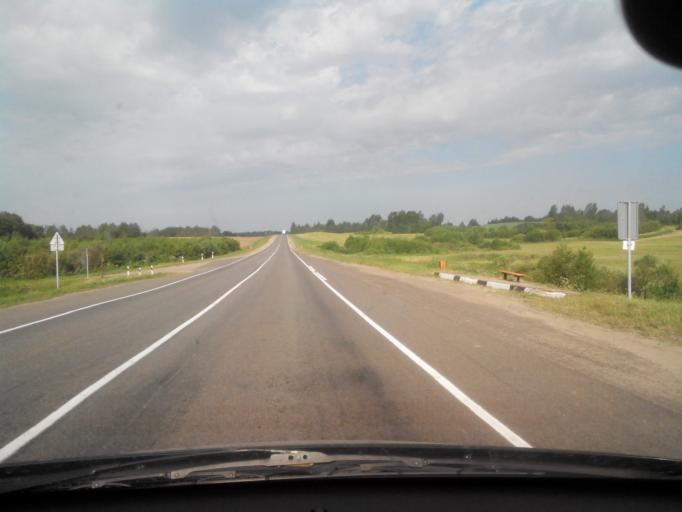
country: BY
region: Minsk
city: Myadzyel
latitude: 55.0641
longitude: 27.1829
